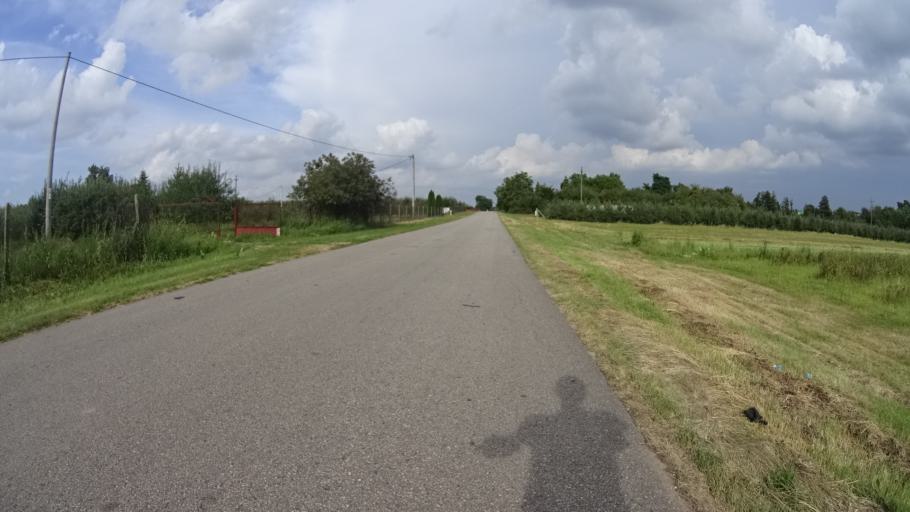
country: PL
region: Masovian Voivodeship
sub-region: Powiat grojecki
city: Goszczyn
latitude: 51.6985
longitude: 20.8389
